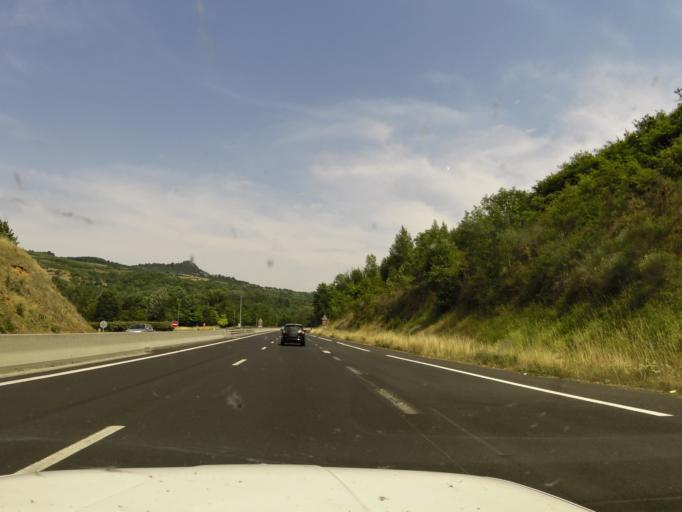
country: FR
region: Auvergne
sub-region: Departement du Puy-de-Dome
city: Vic-le-Comte
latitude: 45.6107
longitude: 3.2132
